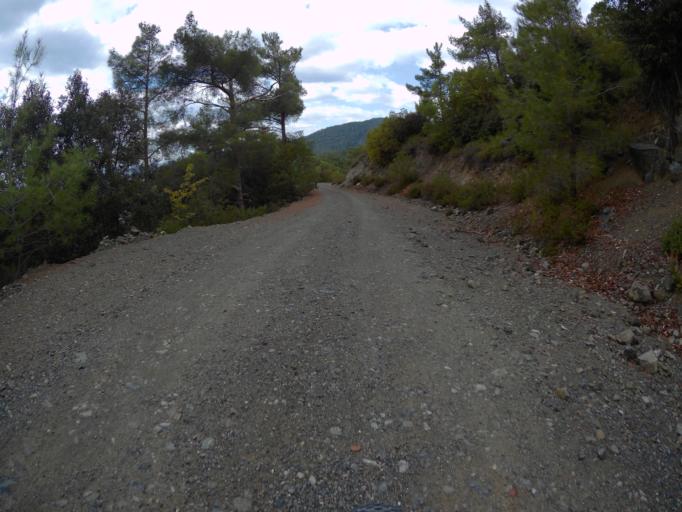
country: CY
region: Lefkosia
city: Kakopetria
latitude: 34.8981
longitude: 32.8479
